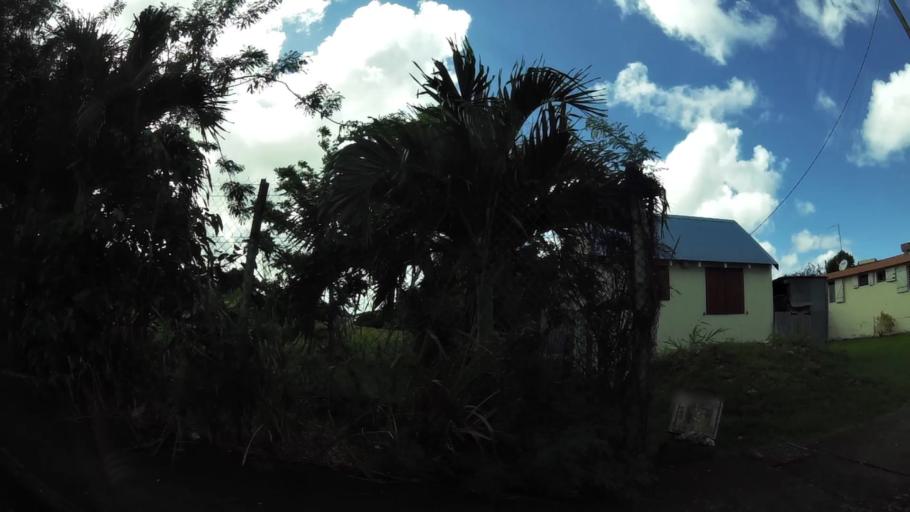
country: GP
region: Guadeloupe
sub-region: Guadeloupe
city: Anse-Bertrand
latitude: 16.4681
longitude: -61.5061
